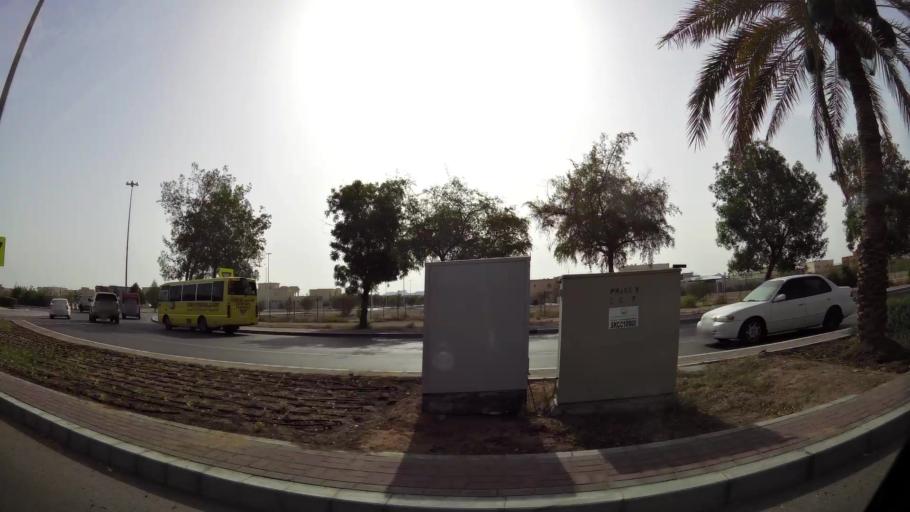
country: AE
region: Abu Dhabi
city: Al Ain
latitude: 24.1521
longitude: 55.7123
